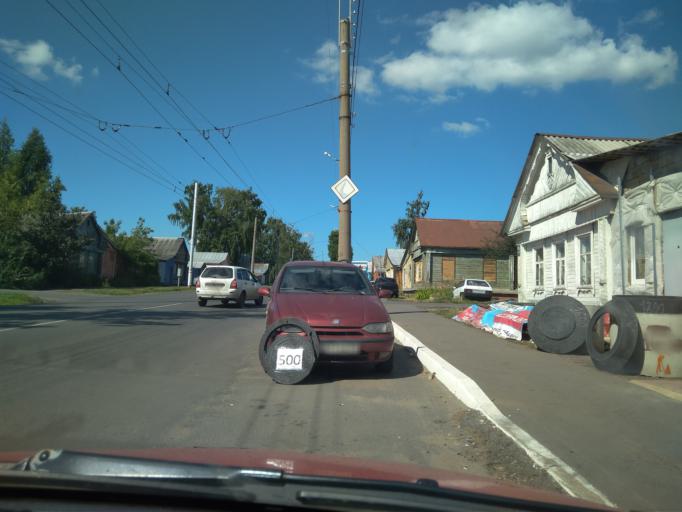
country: RU
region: Mordoviya
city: Nikolayevka
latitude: 54.1650
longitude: 45.1554
